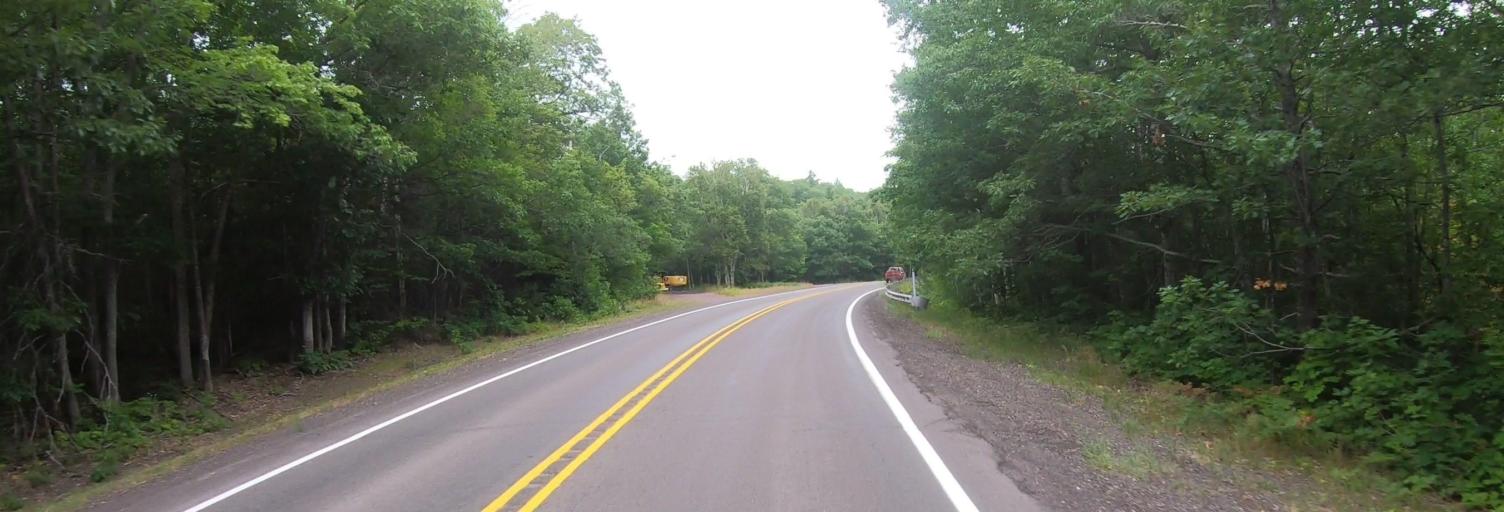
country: US
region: Michigan
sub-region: Keweenaw County
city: Eagle River
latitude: 47.4243
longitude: -88.0796
